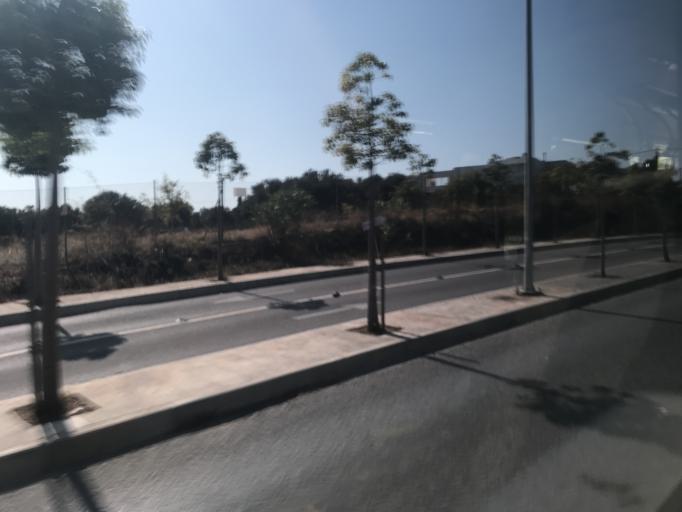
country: GR
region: Crete
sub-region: Nomos Irakleiou
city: Gazi
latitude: 35.3024
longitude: 25.0840
